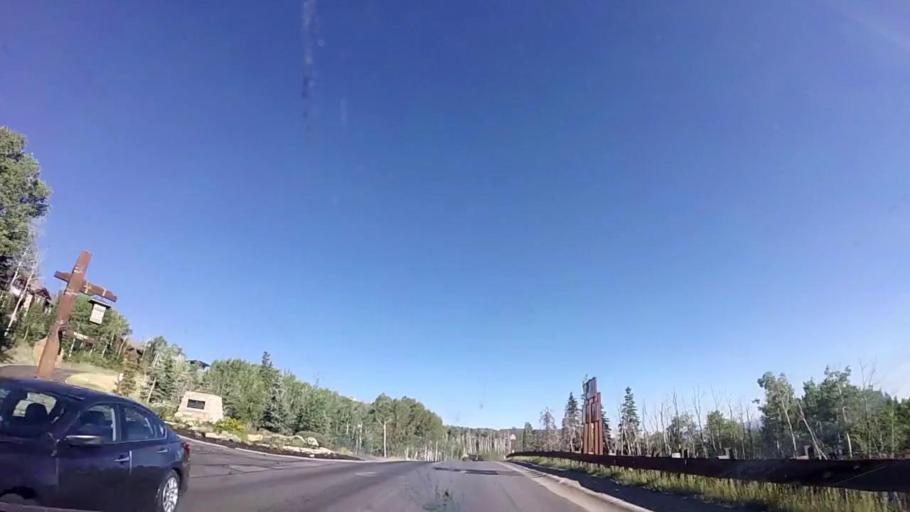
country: US
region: Utah
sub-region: Summit County
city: Park City
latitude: 40.6216
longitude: -111.4973
